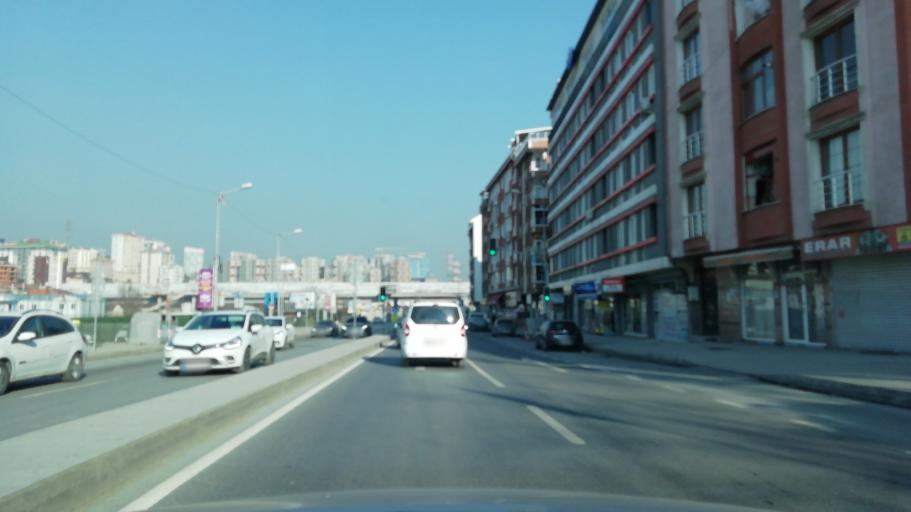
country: TR
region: Istanbul
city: Sisli
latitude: 41.0764
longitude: 28.9500
